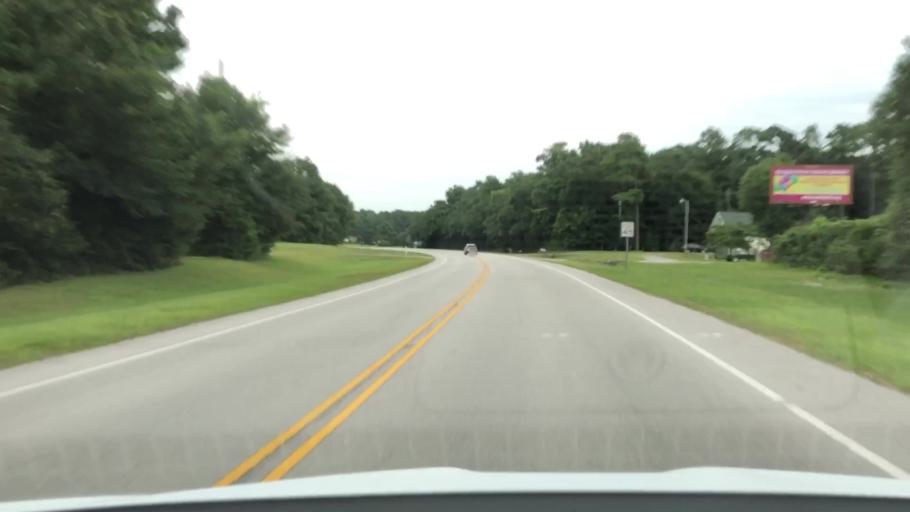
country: US
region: North Carolina
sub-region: Carteret County
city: Cape Carteret
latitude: 34.7014
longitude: -77.0678
